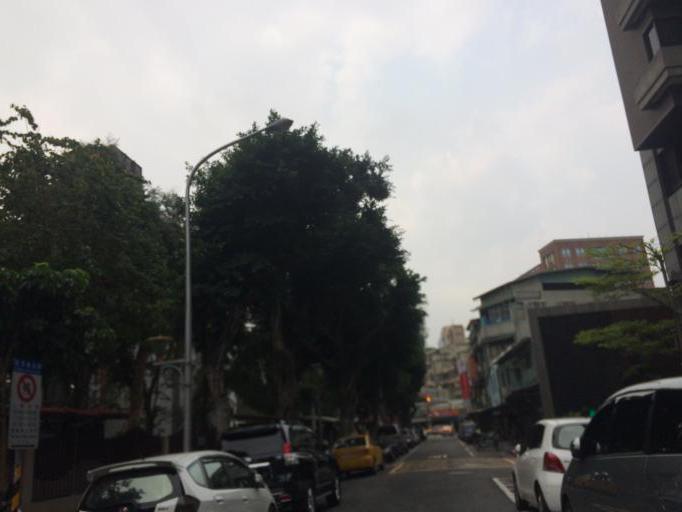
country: TW
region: Taipei
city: Taipei
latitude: 25.0608
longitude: 121.5159
